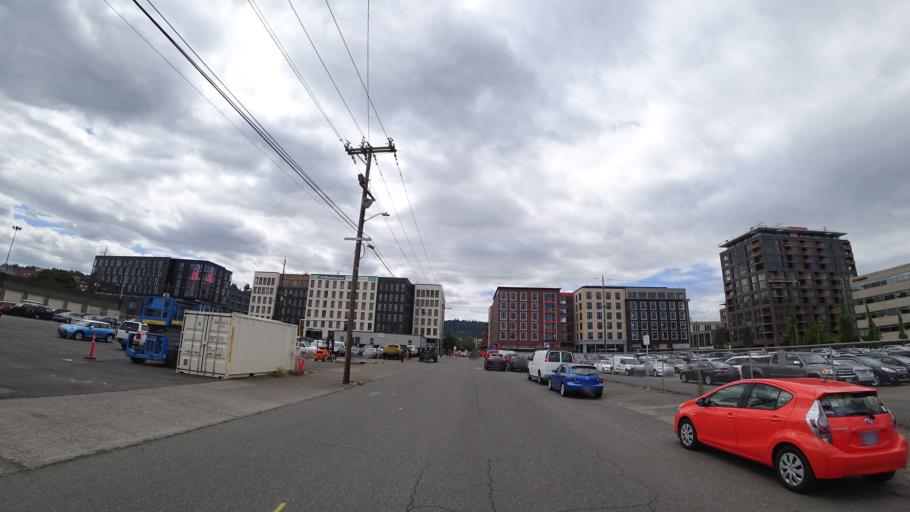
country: US
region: Oregon
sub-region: Multnomah County
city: Portland
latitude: 45.5341
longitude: -122.6935
